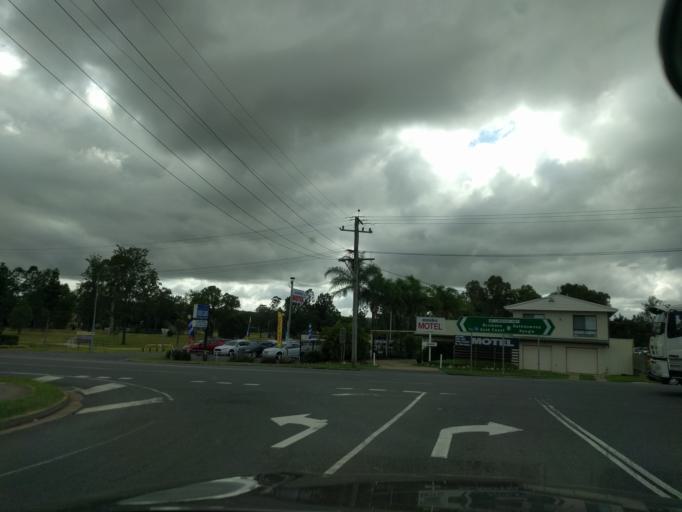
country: AU
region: Queensland
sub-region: Logan
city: Cedar Vale
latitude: -27.9912
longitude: 152.9926
